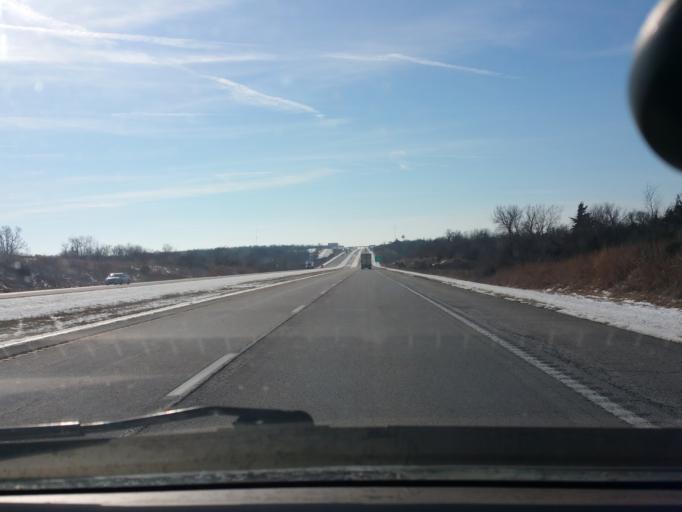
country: US
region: Iowa
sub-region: Decatur County
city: Lamoni
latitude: 40.4875
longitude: -93.9712
